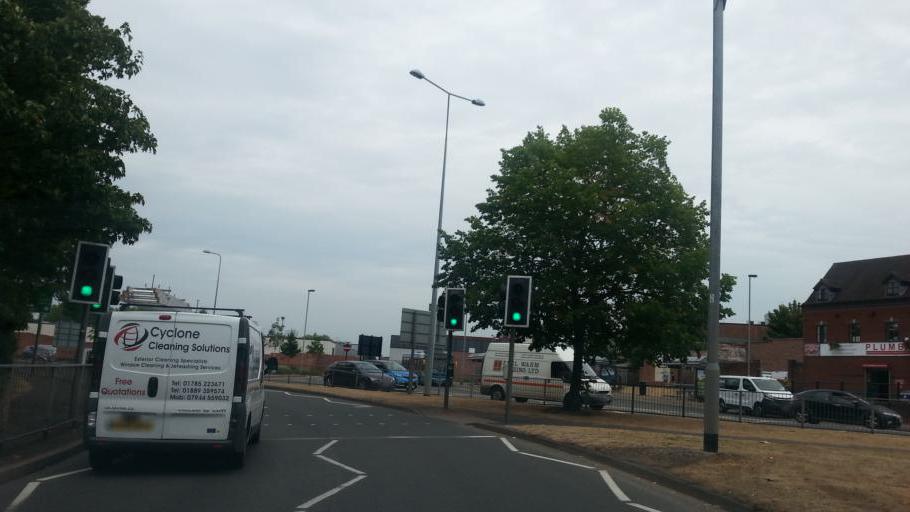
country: GB
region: England
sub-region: Staffordshire
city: Stafford
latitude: 52.8095
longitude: -2.1181
